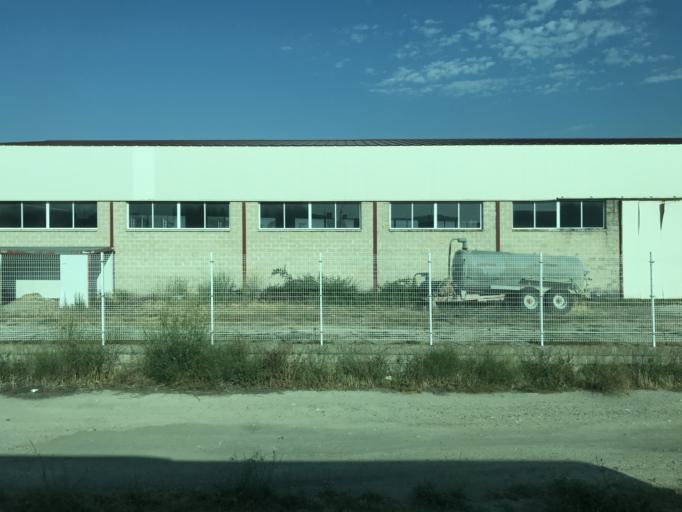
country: ES
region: Castille and Leon
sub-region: Provincia de Valladolid
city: Mojados
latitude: 41.4356
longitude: -4.6669
